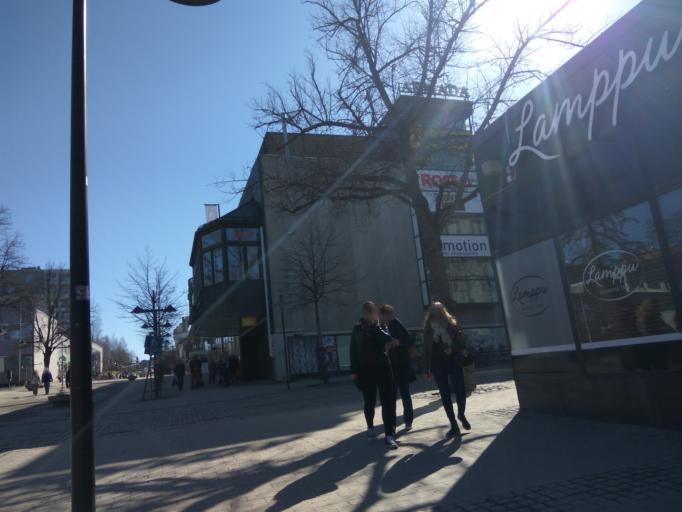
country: FI
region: South Karelia
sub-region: Lappeenranta
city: Lappeenranta
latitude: 61.0599
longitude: 28.1852
